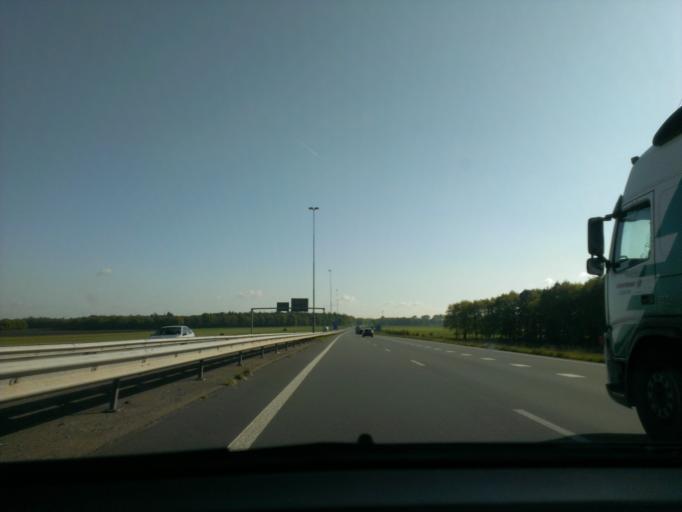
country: NL
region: Drenthe
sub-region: Gemeente Coevorden
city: Sleen
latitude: 52.7329
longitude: 6.7966
